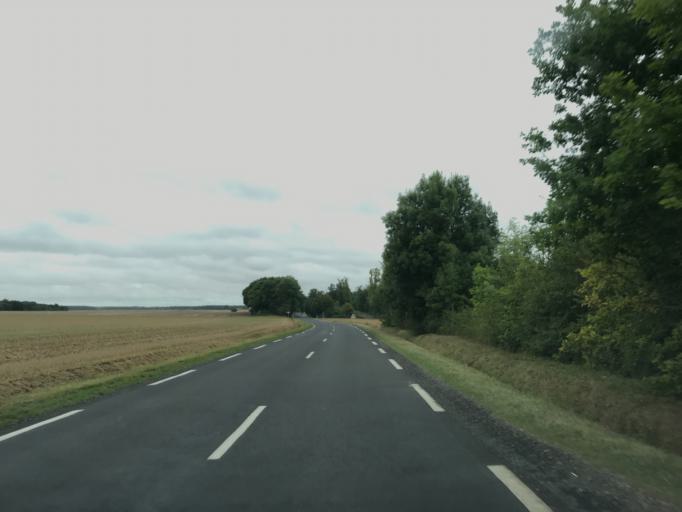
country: FR
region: Haute-Normandie
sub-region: Departement de l'Eure
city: Gravigny
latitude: 49.0223
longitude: 1.2418
